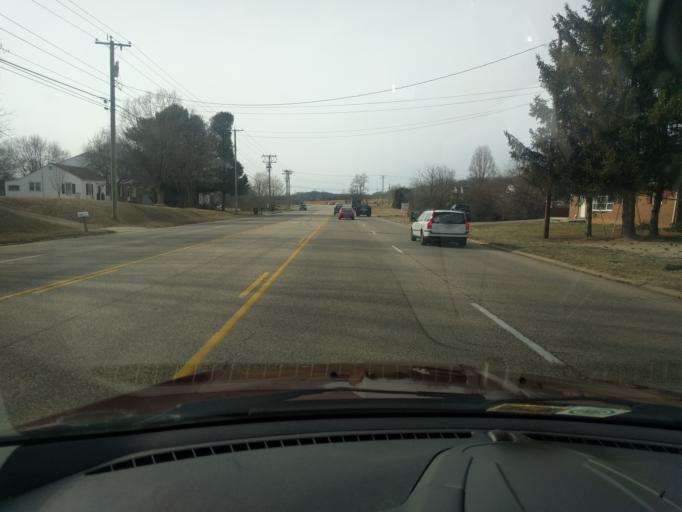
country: US
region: Virginia
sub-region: Augusta County
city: Stuarts Draft
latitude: 38.0421
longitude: -79.0136
